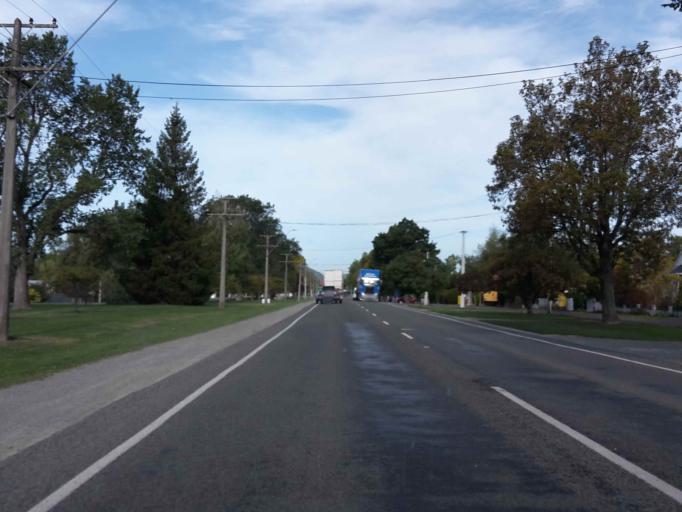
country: NZ
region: Canterbury
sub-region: Timaru District
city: Pleasant Point
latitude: -44.0943
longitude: 170.8247
